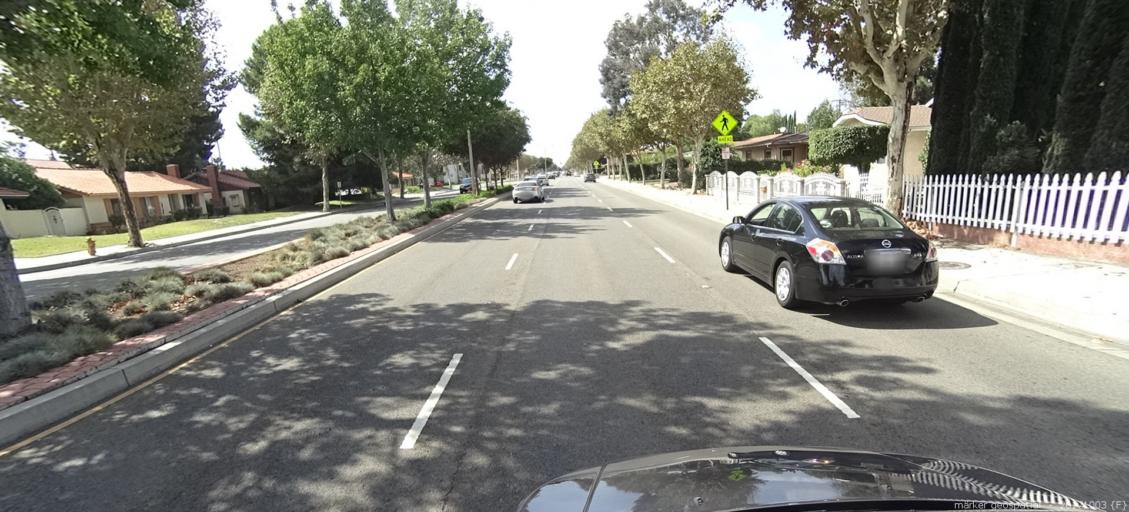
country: US
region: California
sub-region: Orange County
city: Garden Grove
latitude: 33.7744
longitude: -117.9257
